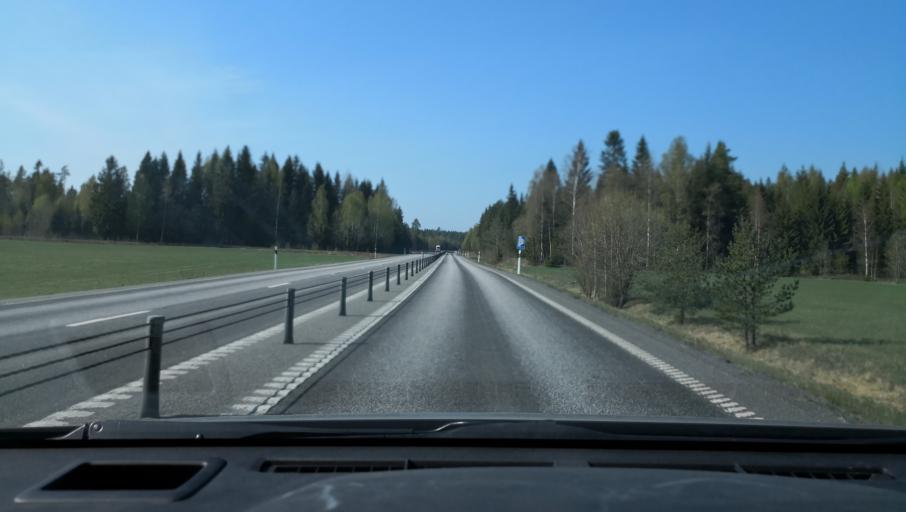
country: SE
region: Uppsala
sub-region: Heby Kommun
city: Tarnsjo
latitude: 60.1748
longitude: 16.9521
